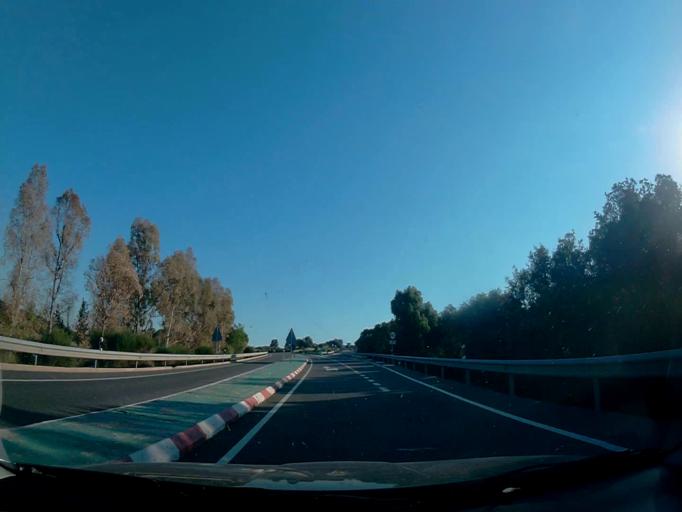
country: ES
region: Castille-La Mancha
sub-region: Province of Toledo
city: Escalona
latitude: 40.1910
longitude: -4.4040
